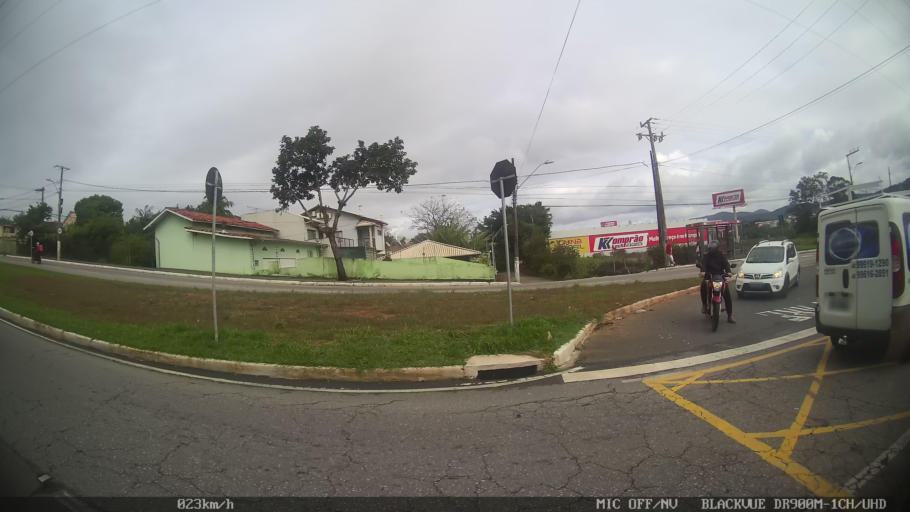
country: BR
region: Santa Catarina
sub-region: Sao Jose
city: Campinas
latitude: -27.5626
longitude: -48.6363
